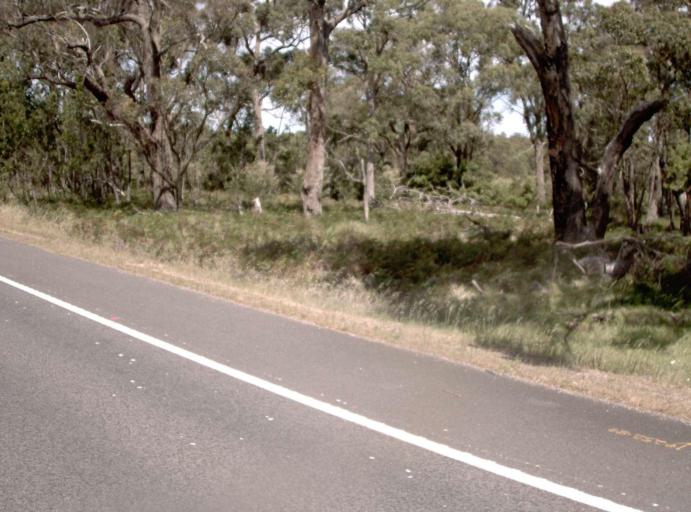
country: AU
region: Victoria
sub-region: East Gippsland
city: Bairnsdale
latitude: -37.9060
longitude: 147.3315
